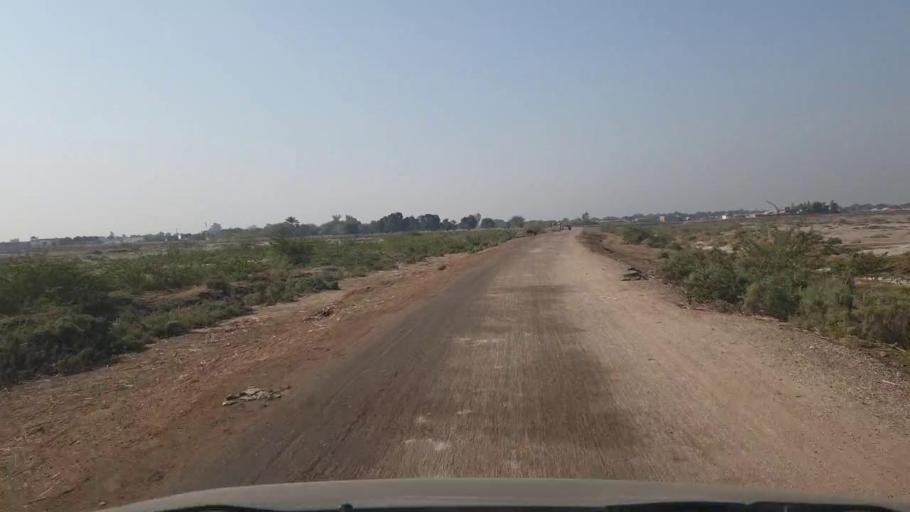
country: PK
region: Sindh
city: Mirwah Gorchani
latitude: 25.2841
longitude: 69.1398
